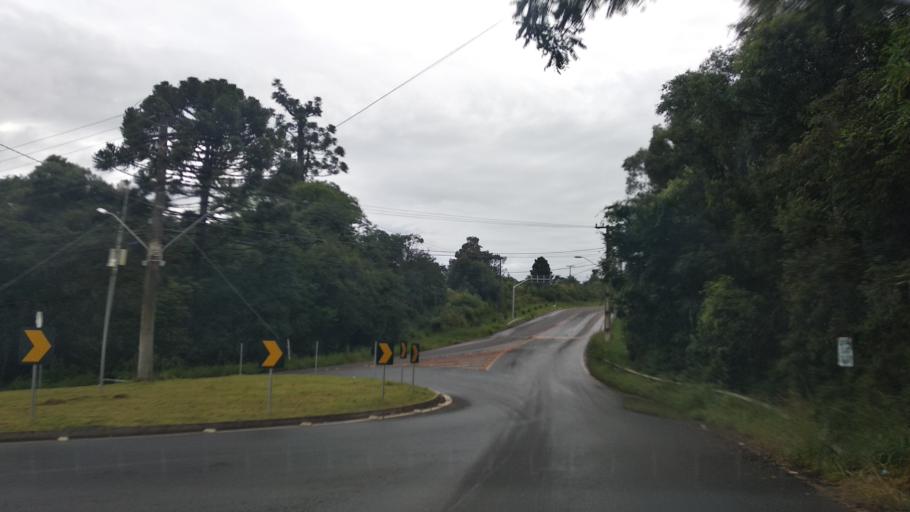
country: BR
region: Santa Catarina
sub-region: Videira
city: Videira
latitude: -27.0326
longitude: -51.1554
